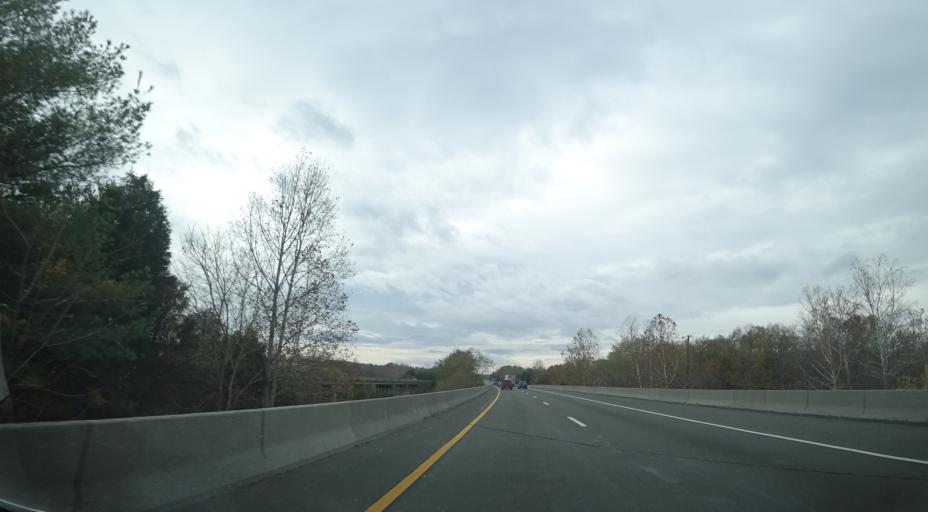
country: US
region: Virginia
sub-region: Fauquier County
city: New Baltimore
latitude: 38.8477
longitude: -77.7606
